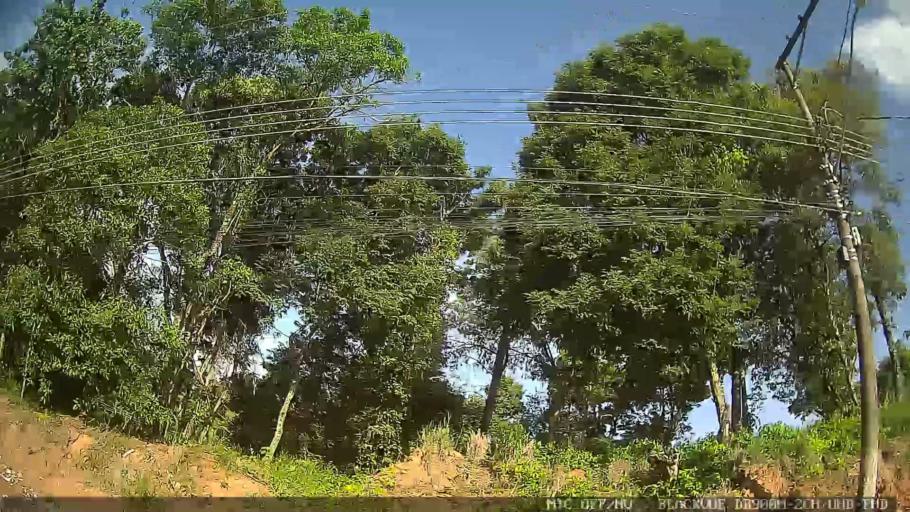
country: BR
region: Sao Paulo
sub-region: Serra Negra
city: Serra Negra
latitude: -22.6367
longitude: -46.6992
